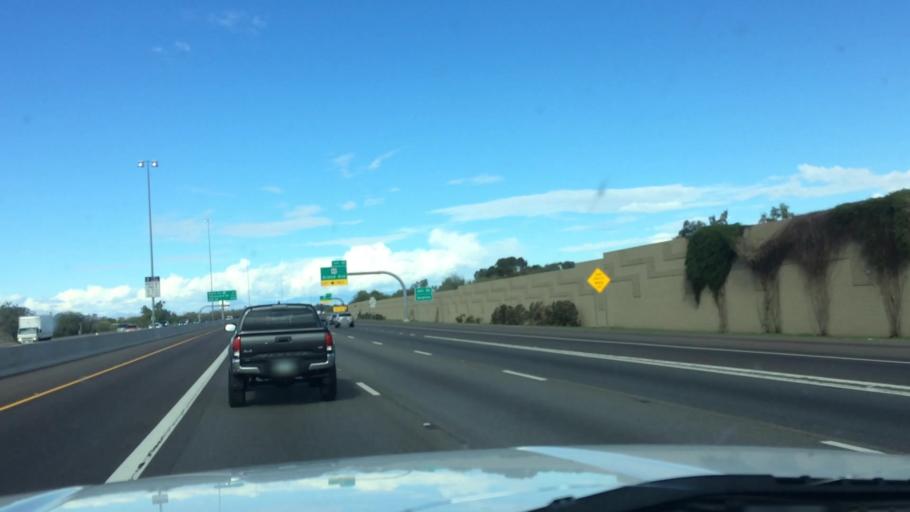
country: US
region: Arizona
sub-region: Maricopa County
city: Sun City
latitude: 33.5837
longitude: -112.2616
